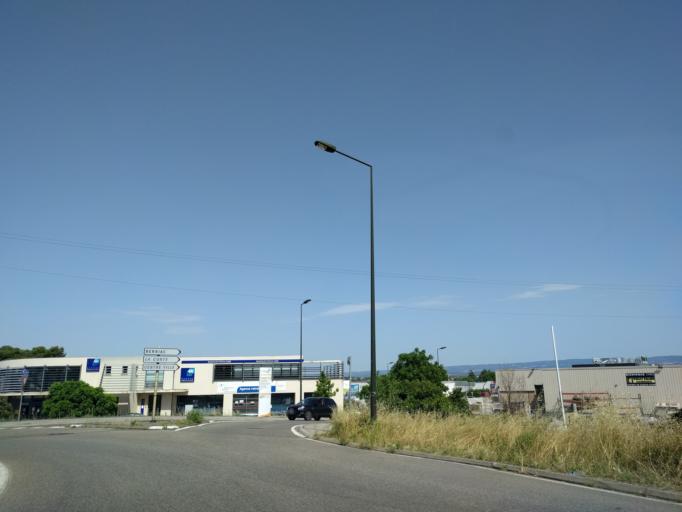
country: FR
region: Languedoc-Roussillon
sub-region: Departement de l'Aude
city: Palaja
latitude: 43.2077
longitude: 2.3877
